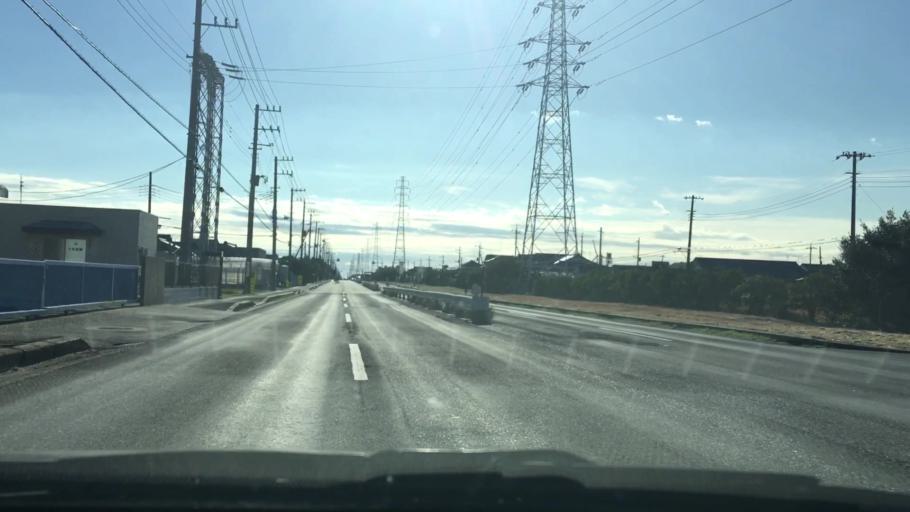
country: JP
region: Chiba
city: Omigawa
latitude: 35.8747
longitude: 140.7201
